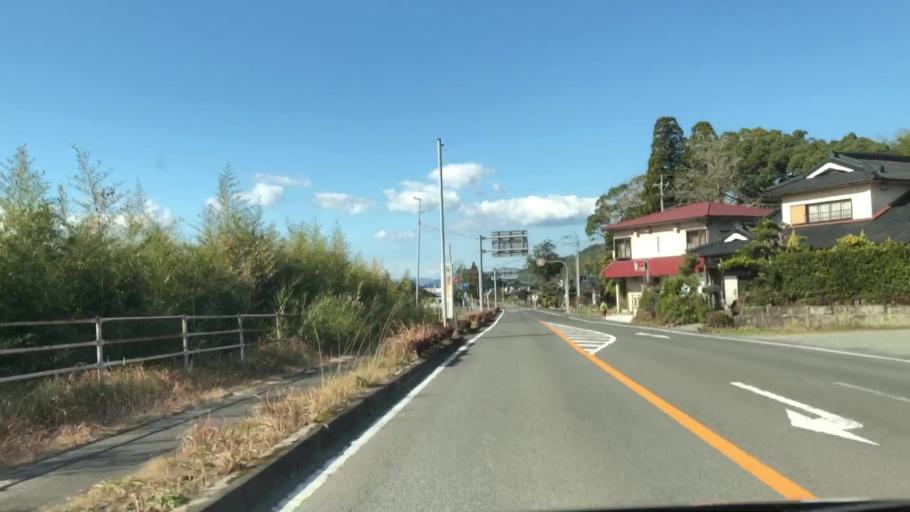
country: JP
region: Kagoshima
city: Satsumasendai
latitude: 31.7960
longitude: 130.4418
